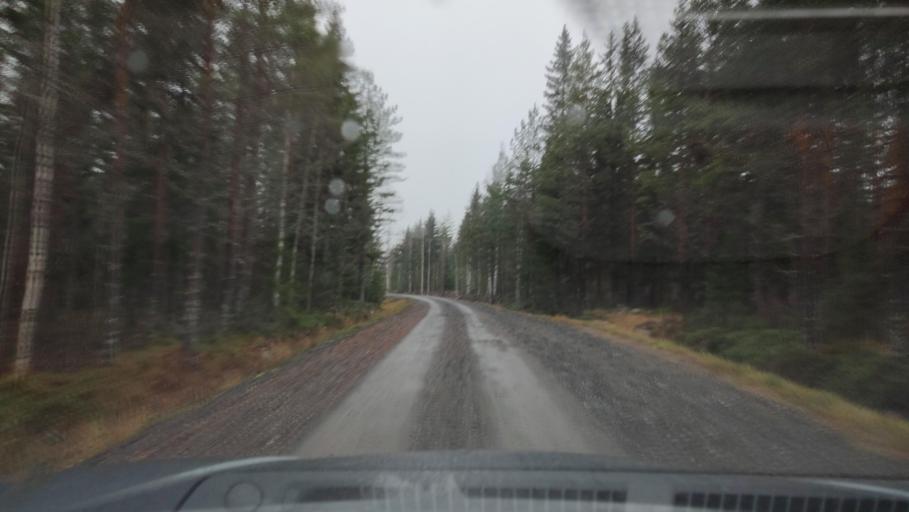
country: FI
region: Southern Ostrobothnia
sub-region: Suupohja
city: Karijoki
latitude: 62.1785
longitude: 21.6953
